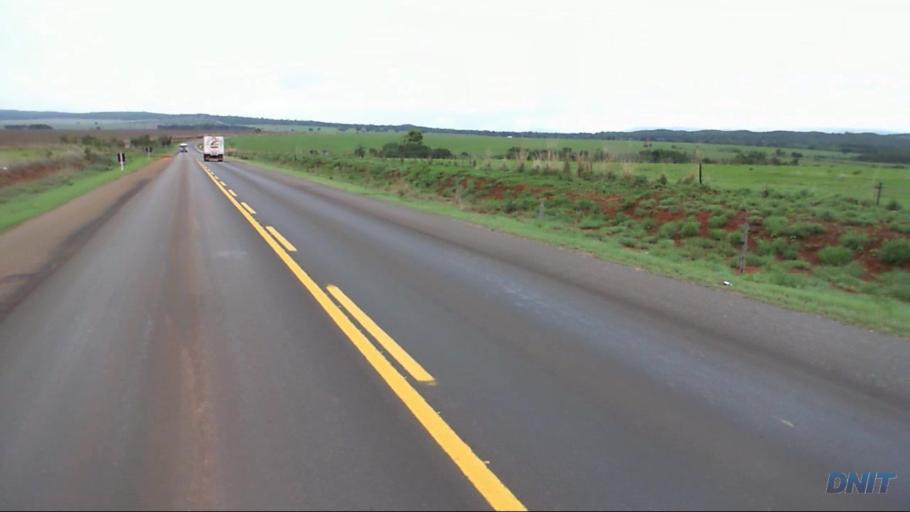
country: BR
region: Goias
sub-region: Padre Bernardo
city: Padre Bernardo
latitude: -15.1742
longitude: -48.3736
